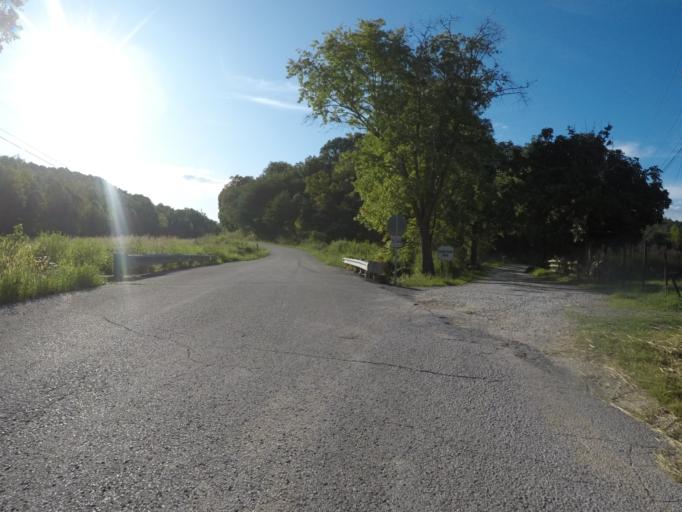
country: US
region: West Virginia
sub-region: Cabell County
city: Huntington
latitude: 38.5214
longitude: -82.5029
